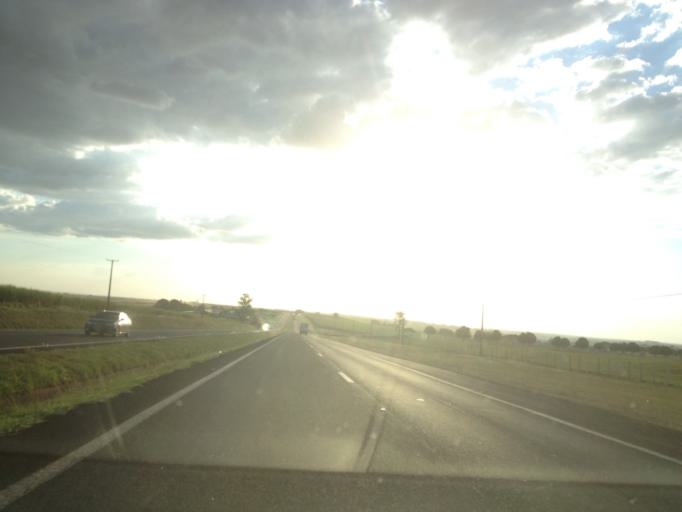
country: BR
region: Sao Paulo
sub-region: Jau
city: Jau
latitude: -22.2711
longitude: -48.4737
